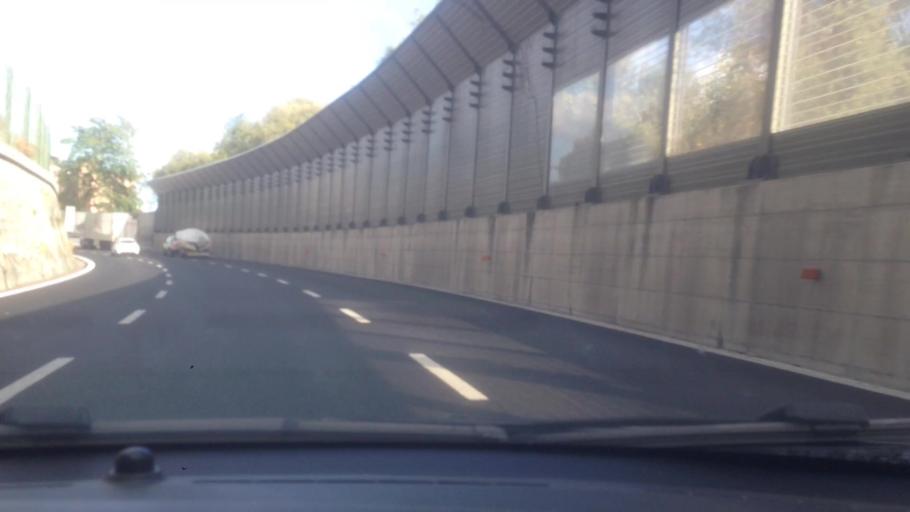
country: IT
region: Liguria
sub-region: Provincia di Genova
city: Cogoleto
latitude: 44.3917
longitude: 8.6460
